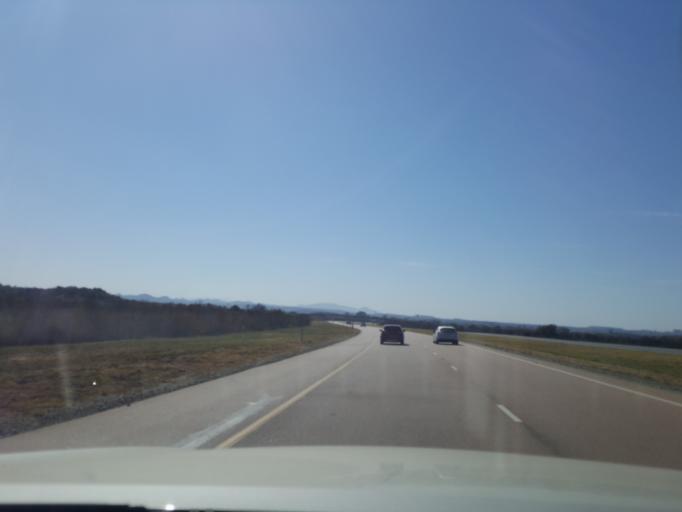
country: ZA
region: North-West
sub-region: Bojanala Platinum District Municipality
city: Brits
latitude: -25.7448
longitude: 27.5297
